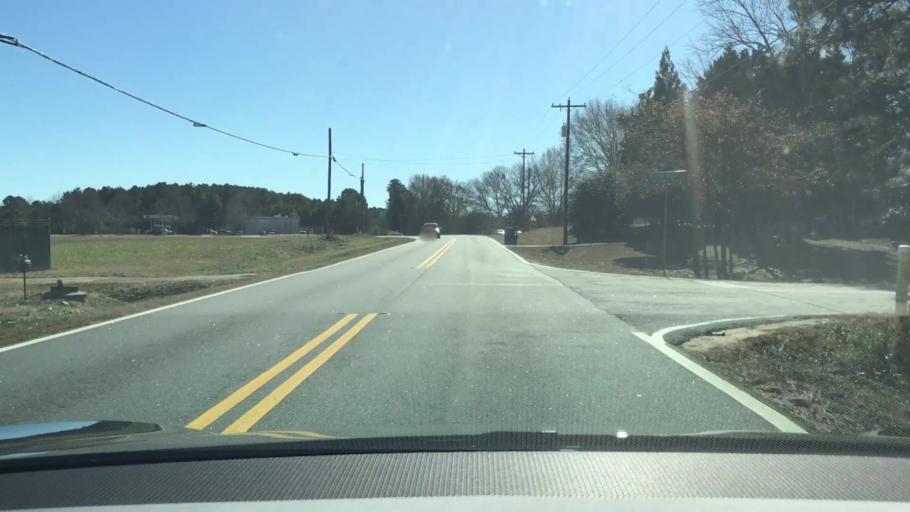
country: US
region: Georgia
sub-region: Walton County
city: Monroe
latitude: 33.8347
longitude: -83.7342
